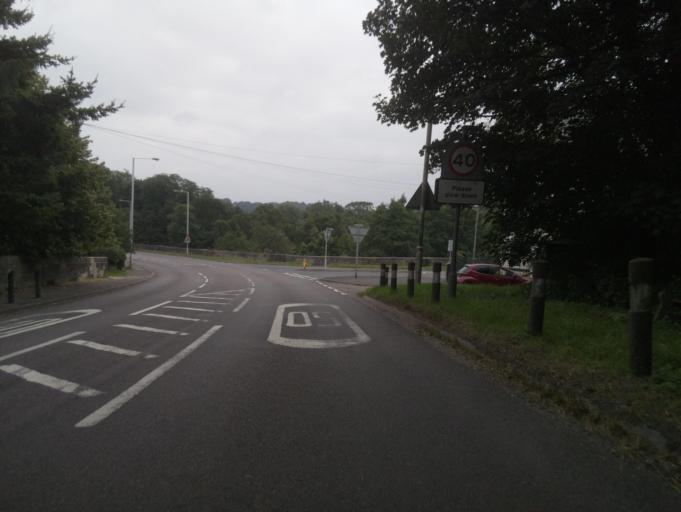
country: GB
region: England
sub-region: Staffordshire
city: Mayfield
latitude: 53.0100
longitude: -1.7662
